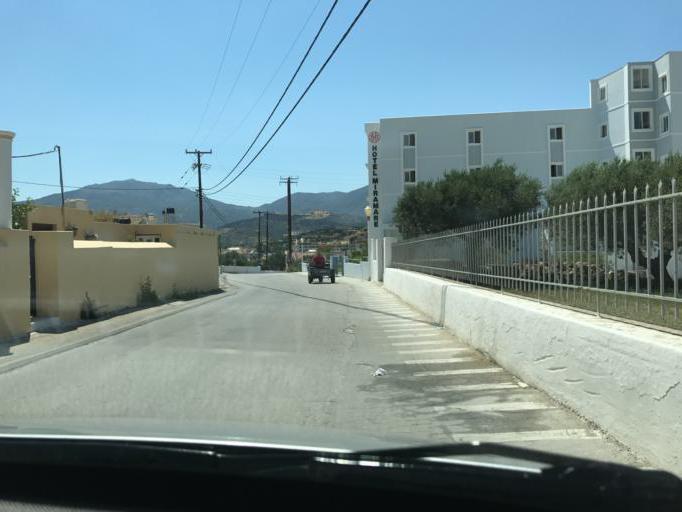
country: GR
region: South Aegean
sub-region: Nomos Dodekanisou
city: Karpathos
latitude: 35.5076
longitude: 27.2072
